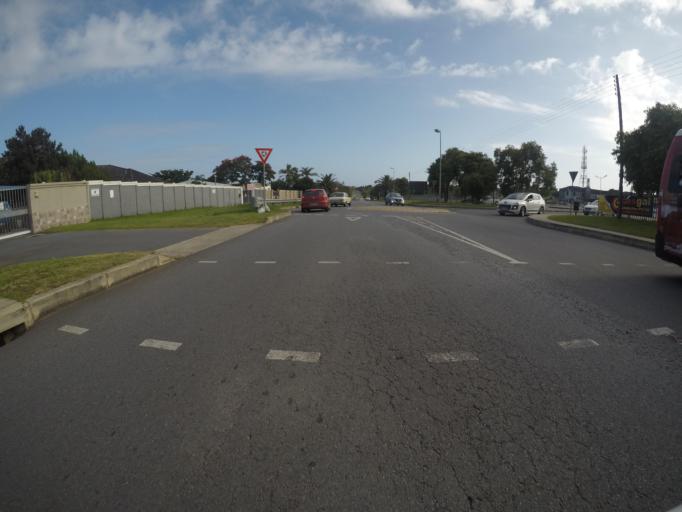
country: ZA
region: Eastern Cape
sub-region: Buffalo City Metropolitan Municipality
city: East London
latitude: -32.9675
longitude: 27.9415
